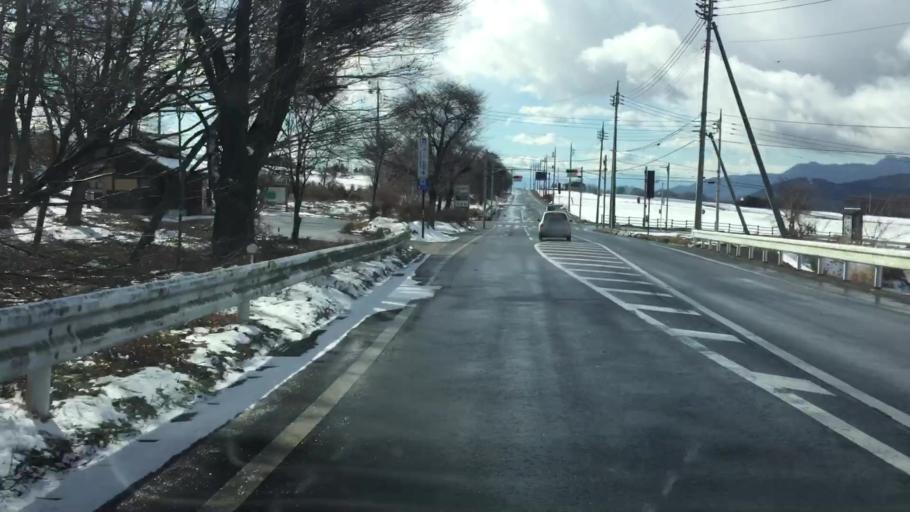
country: JP
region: Gunma
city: Numata
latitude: 36.6112
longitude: 139.0790
